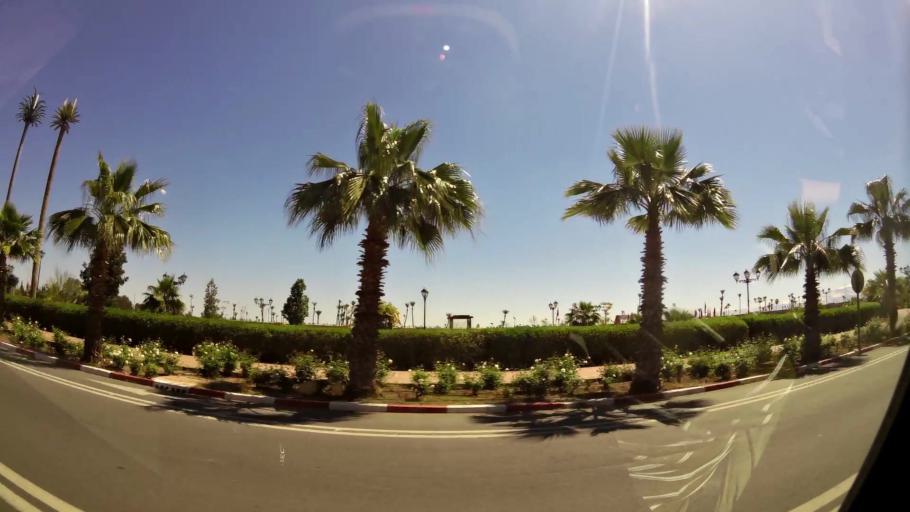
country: MA
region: Marrakech-Tensift-Al Haouz
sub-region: Marrakech
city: Marrakesh
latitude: 31.5975
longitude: -7.9868
